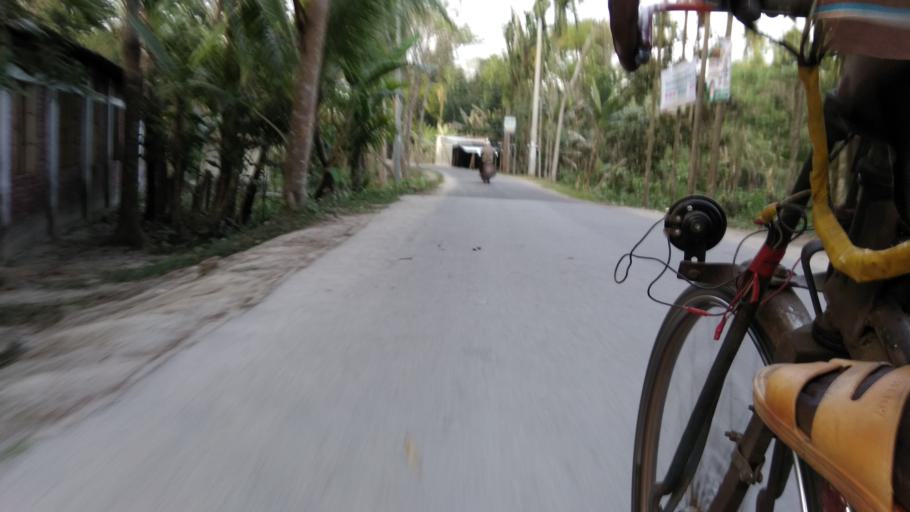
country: BD
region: Barisal
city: Mehendiganj
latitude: 22.9371
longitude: 90.4074
